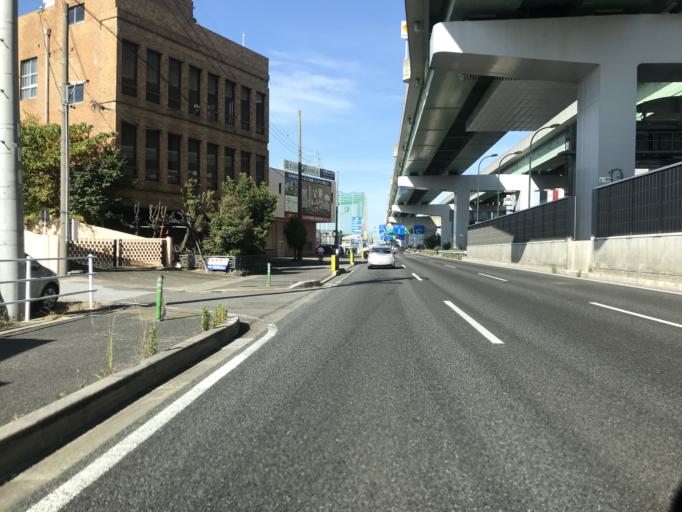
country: JP
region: Aichi
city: Iwakura
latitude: 35.2538
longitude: 136.8432
